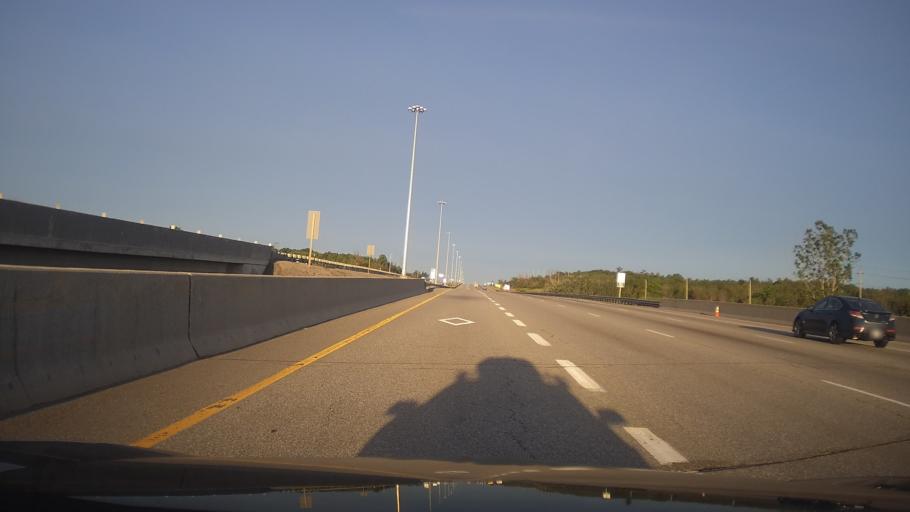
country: CA
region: Ontario
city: Bells Corners
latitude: 45.3313
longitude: -75.8596
